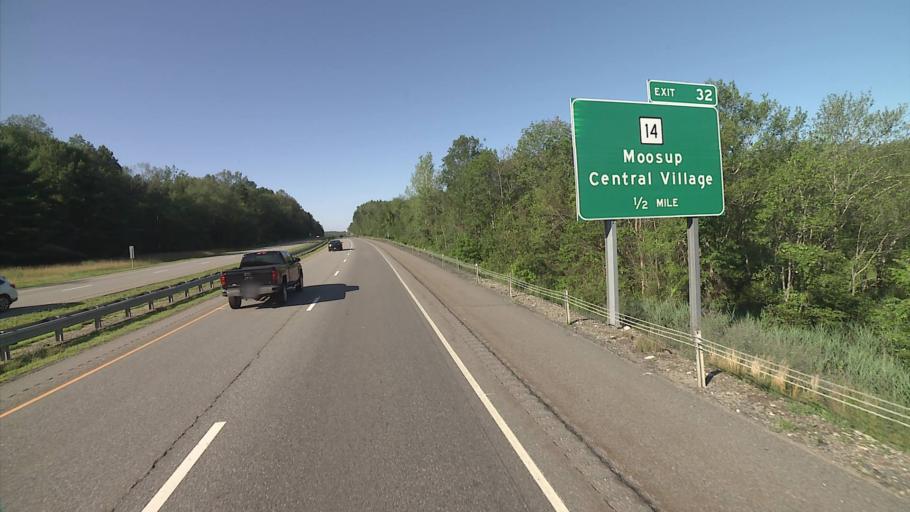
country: US
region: Connecticut
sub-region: Windham County
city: Moosup
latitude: 41.7290
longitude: -71.8894
